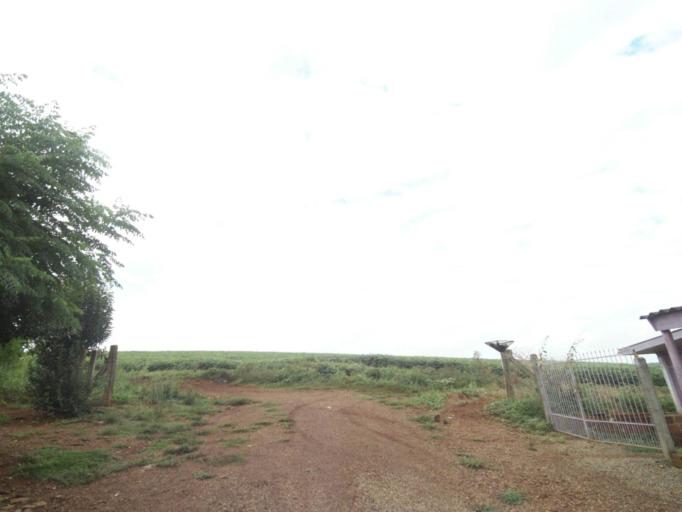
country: BR
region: Rio Grande do Sul
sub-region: Lagoa Vermelha
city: Lagoa Vermelha
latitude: -28.2233
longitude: -51.5253
